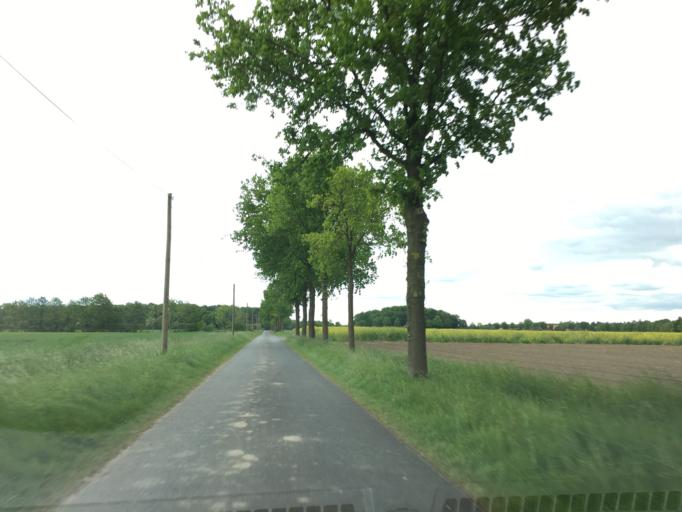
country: DE
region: North Rhine-Westphalia
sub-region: Regierungsbezirk Munster
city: Senden
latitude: 51.8982
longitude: 7.5660
